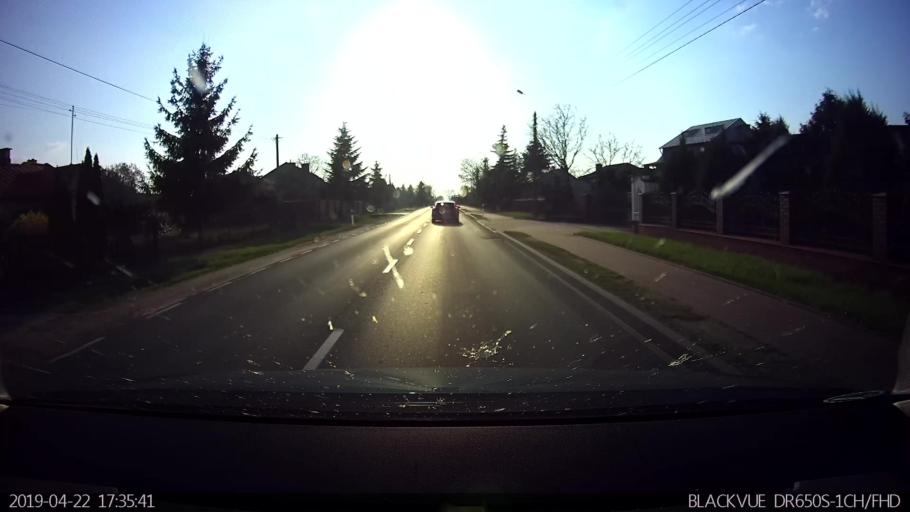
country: PL
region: Masovian Voivodeship
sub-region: Powiat sokolowski
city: Sokolow Podlaski
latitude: 52.4075
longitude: 22.2004
